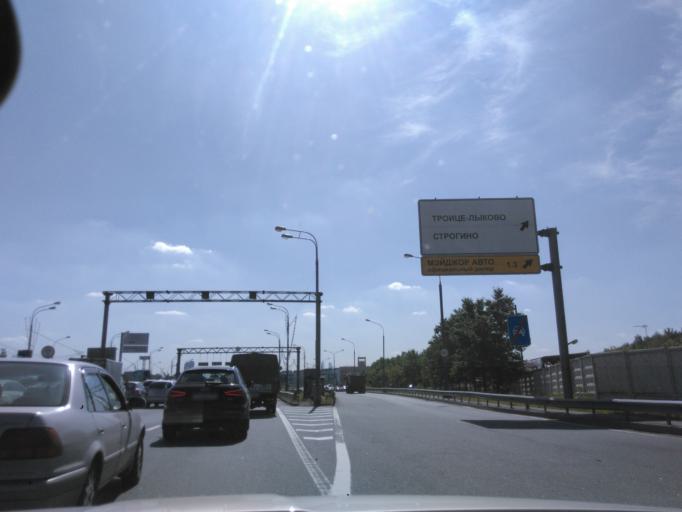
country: RU
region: Moscow
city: Rublevo
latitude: 55.7879
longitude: 37.3819
